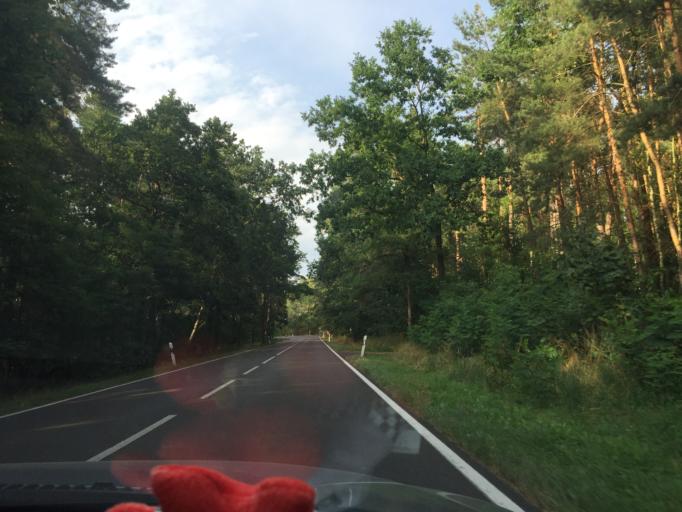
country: DE
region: Brandenburg
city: Liebenwalde
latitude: 52.9290
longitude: 13.3891
